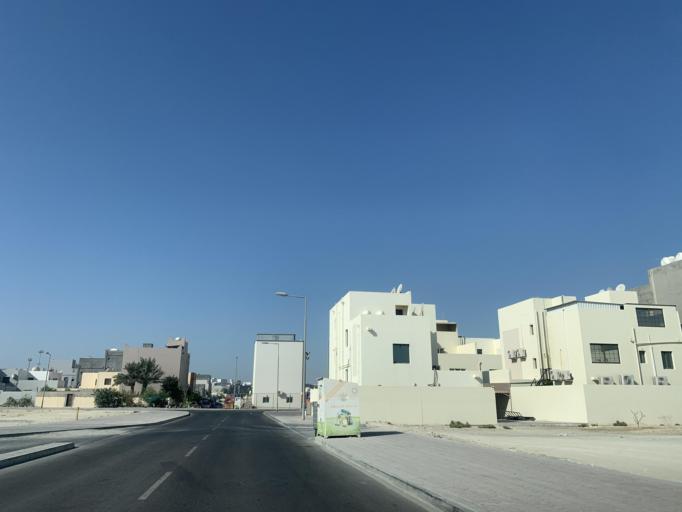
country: BH
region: Central Governorate
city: Madinat Hamad
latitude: 26.1249
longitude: 50.4826
